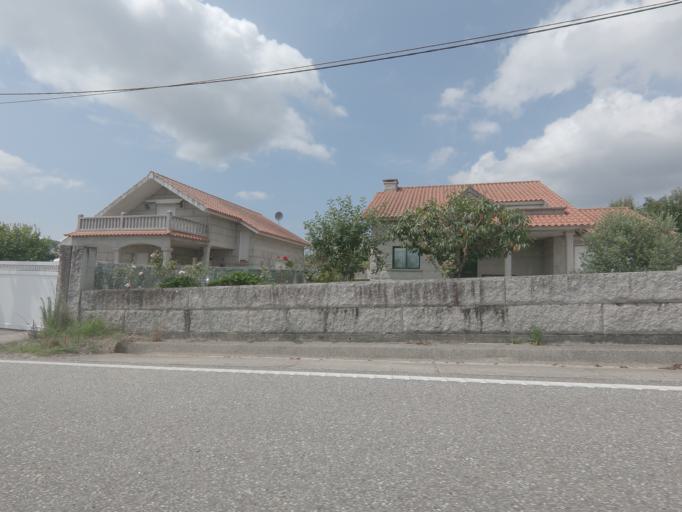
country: PT
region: Viana do Castelo
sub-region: Valenca
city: Valenca
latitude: 42.0228
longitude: -8.6846
